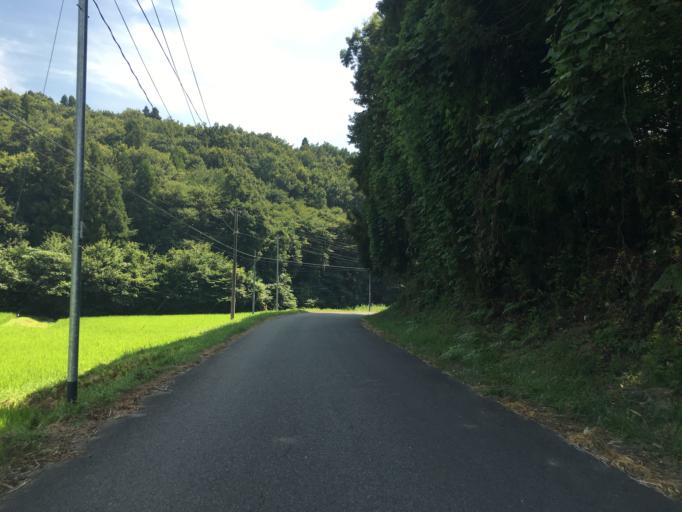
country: JP
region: Fukushima
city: Ishikawa
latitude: 37.1997
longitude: 140.4778
